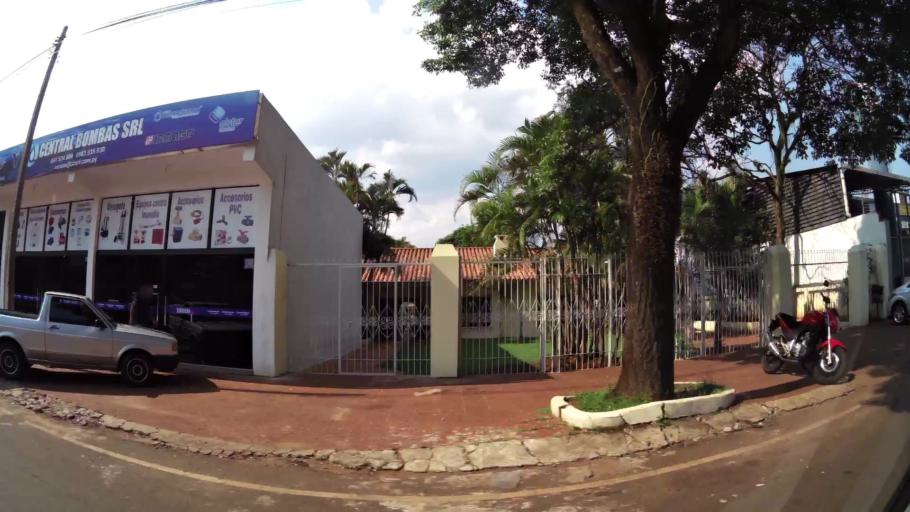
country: PY
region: Alto Parana
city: Ciudad del Este
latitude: -25.5067
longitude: -54.6352
